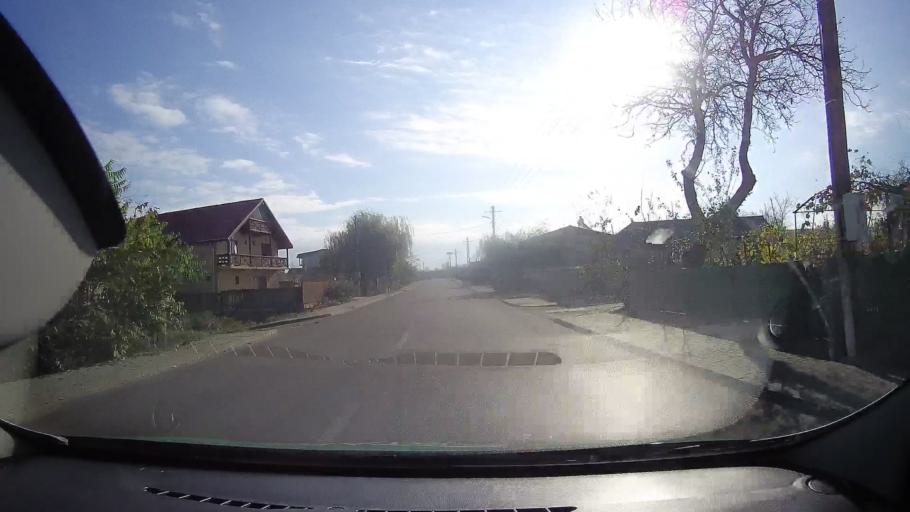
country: RO
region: Tulcea
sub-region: Comuna Murighiol
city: Murighiol
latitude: 45.0397
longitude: 29.1580
